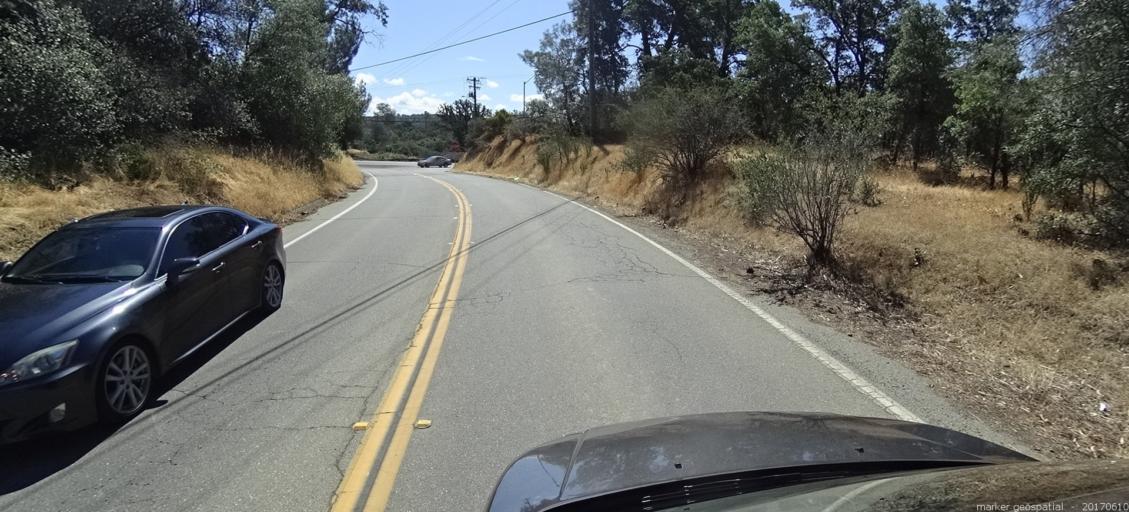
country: US
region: California
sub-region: Butte County
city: Oroville East
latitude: 39.5050
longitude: -121.4993
